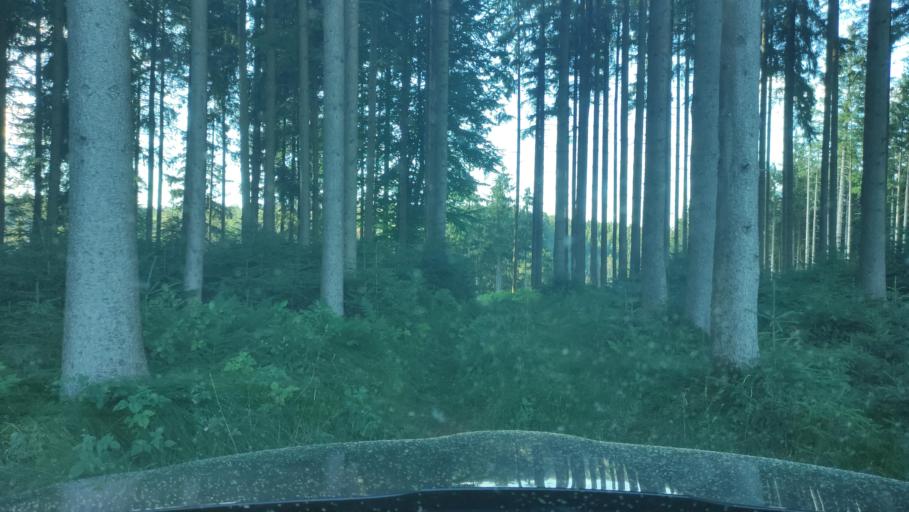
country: DE
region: Bavaria
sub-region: Swabia
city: Krumbach
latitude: 48.2558
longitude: 10.3479
